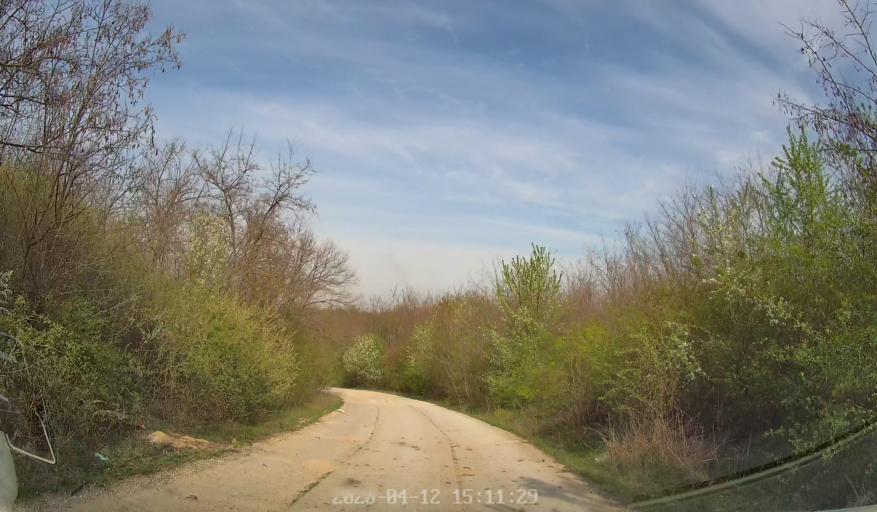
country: MD
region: Telenesti
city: Cocieri
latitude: 47.3253
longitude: 29.0704
